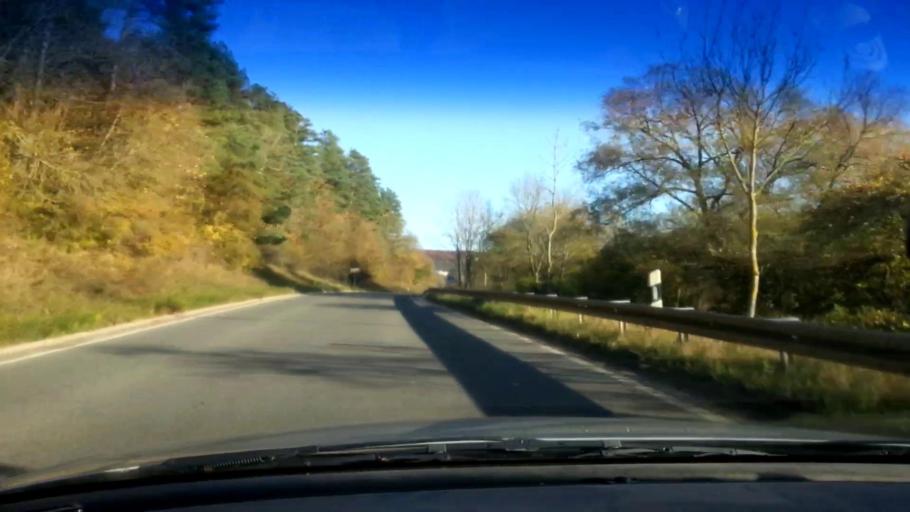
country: DE
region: Bavaria
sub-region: Upper Franconia
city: Heiligenstadt
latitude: 49.8688
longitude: 11.1566
